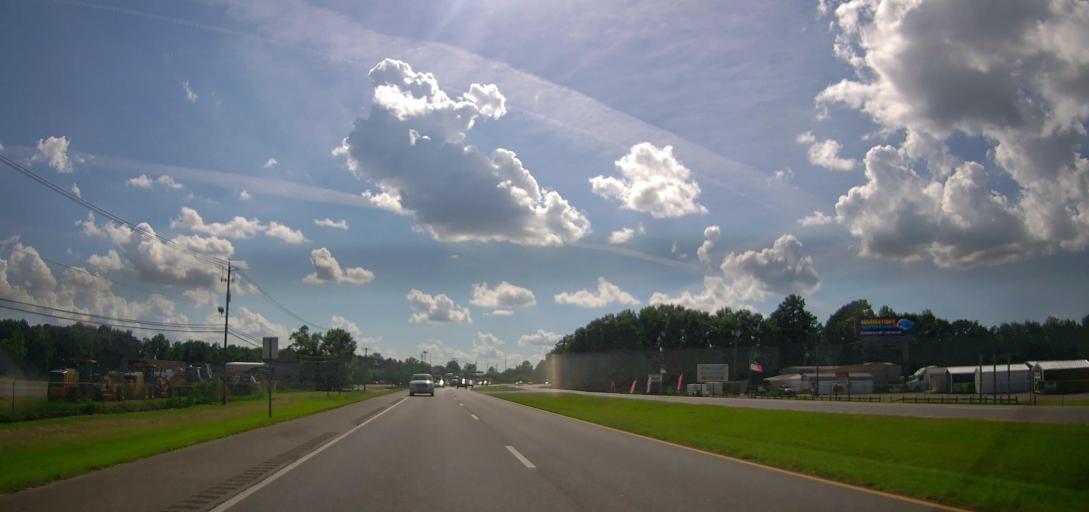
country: US
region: Alabama
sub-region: Tuscaloosa County
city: Northport
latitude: 33.2331
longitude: -87.6218
